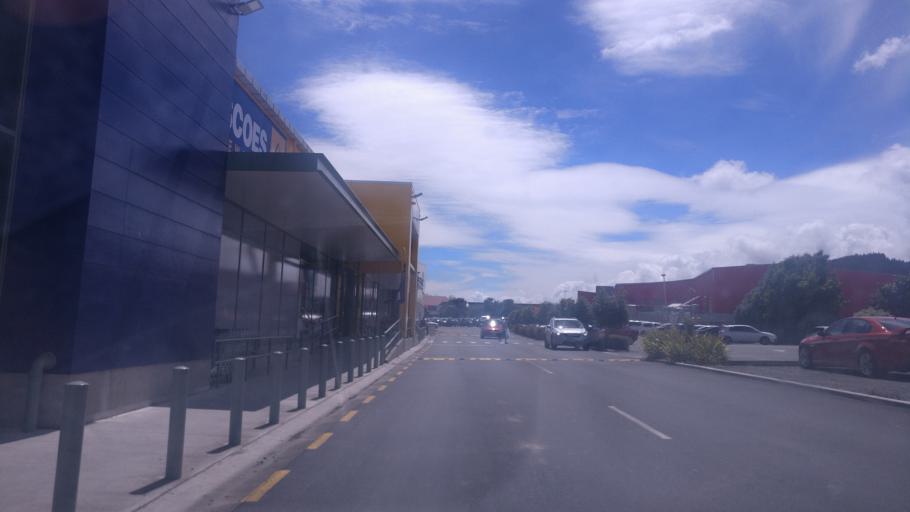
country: NZ
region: Wellington
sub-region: Kapiti Coast District
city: Paraparaumu
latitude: -40.9203
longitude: 175.0024
